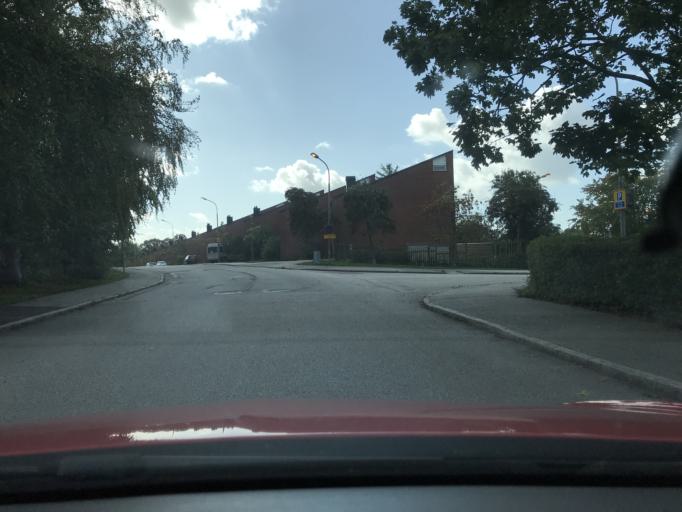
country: SE
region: Skane
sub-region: Lunds Kommun
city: Lund
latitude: 55.7192
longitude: 13.1892
